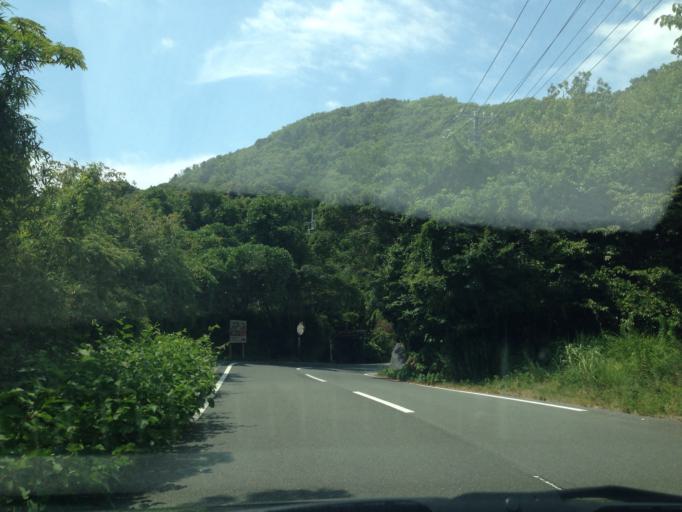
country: JP
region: Shizuoka
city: Shimoda
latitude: 34.6339
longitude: 138.8155
